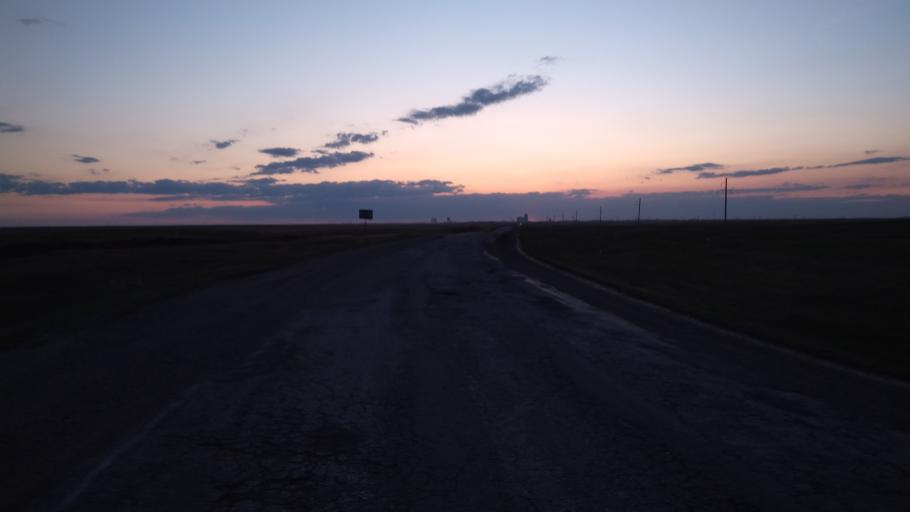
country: RU
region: Chelyabinsk
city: Troitsk
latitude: 54.0872
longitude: 61.6576
